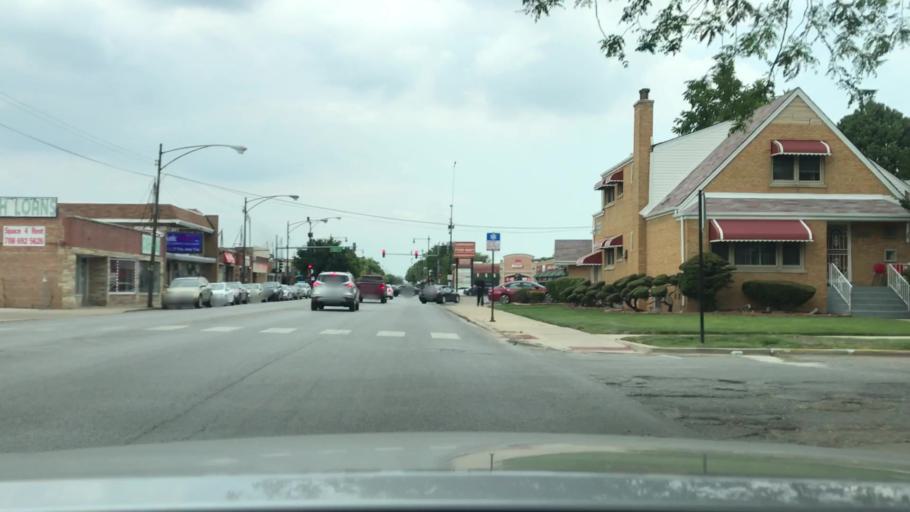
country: US
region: Illinois
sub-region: Cook County
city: Evergreen Park
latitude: 41.7415
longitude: -87.7021
